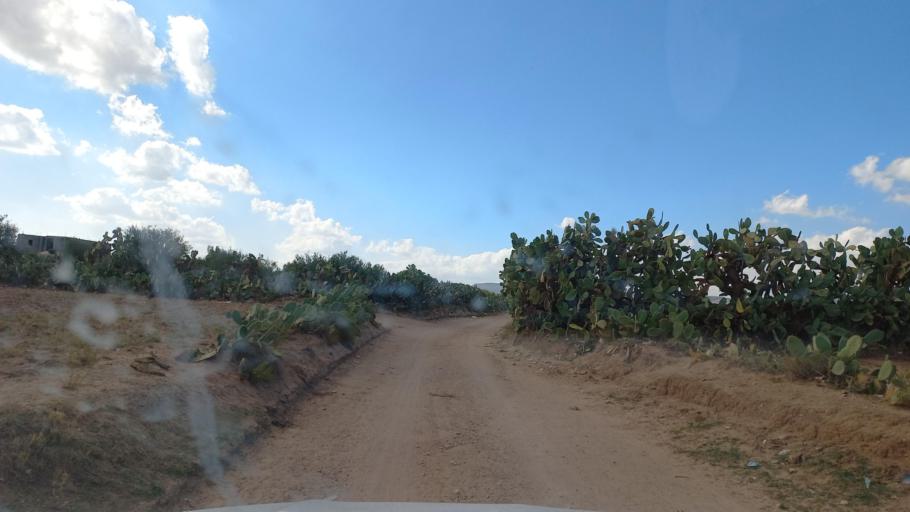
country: TN
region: Al Qasrayn
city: Sbiba
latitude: 35.3863
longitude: 9.0440
